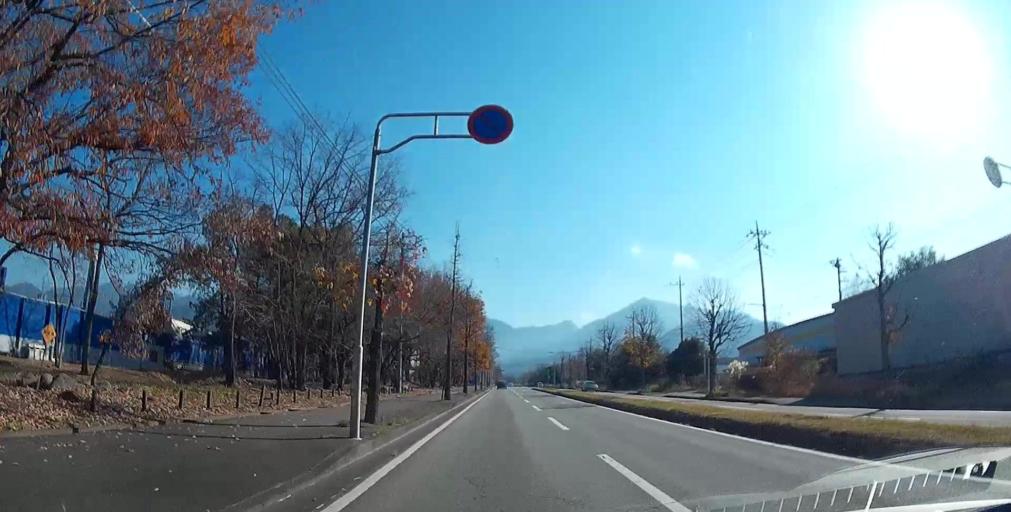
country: JP
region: Yamanashi
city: Isawa
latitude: 35.6282
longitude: 138.6835
